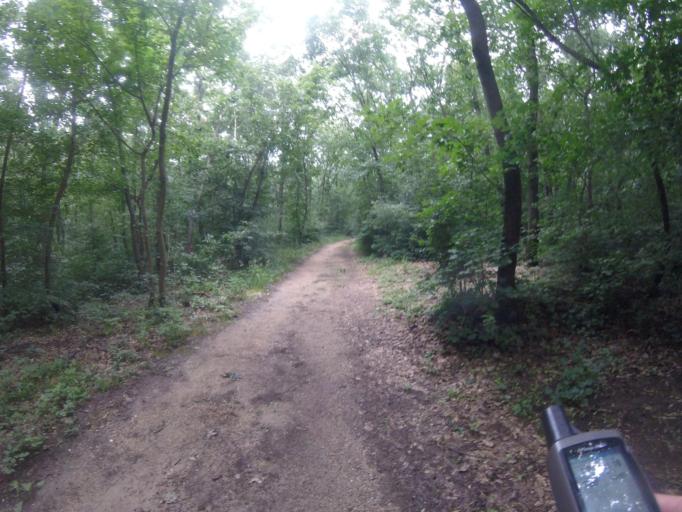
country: HU
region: Pest
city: Toeroekbalint
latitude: 47.4238
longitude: 18.9066
